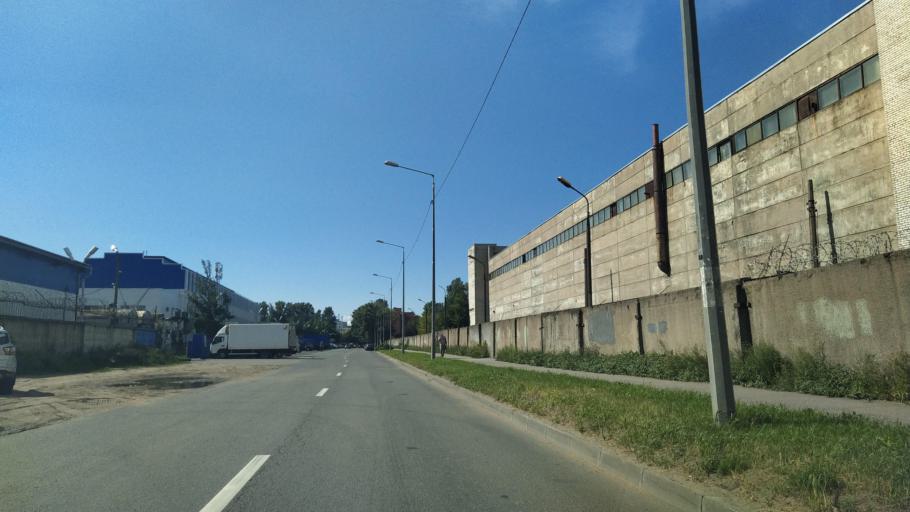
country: RU
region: Leningrad
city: Finlyandskiy
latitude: 59.9751
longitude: 30.3578
